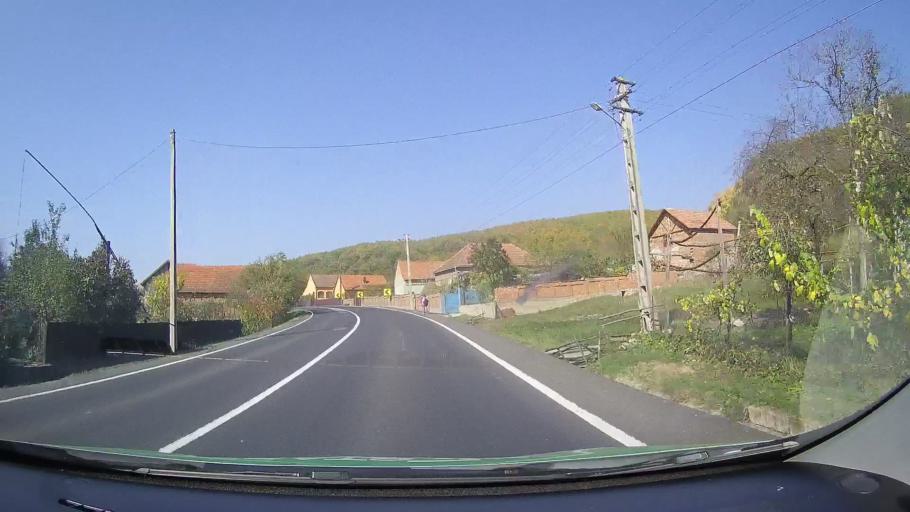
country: RO
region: Hunedoara
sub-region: Comuna Dobra
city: Dobra
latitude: 45.9392
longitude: 22.5403
